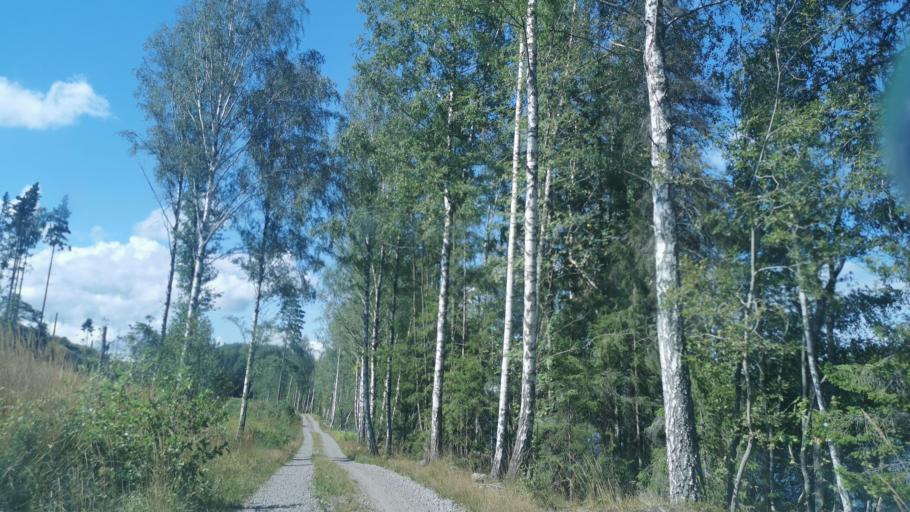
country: SE
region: OEstergoetland
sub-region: Finspangs Kommun
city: Finspang
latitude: 58.7933
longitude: 15.8292
